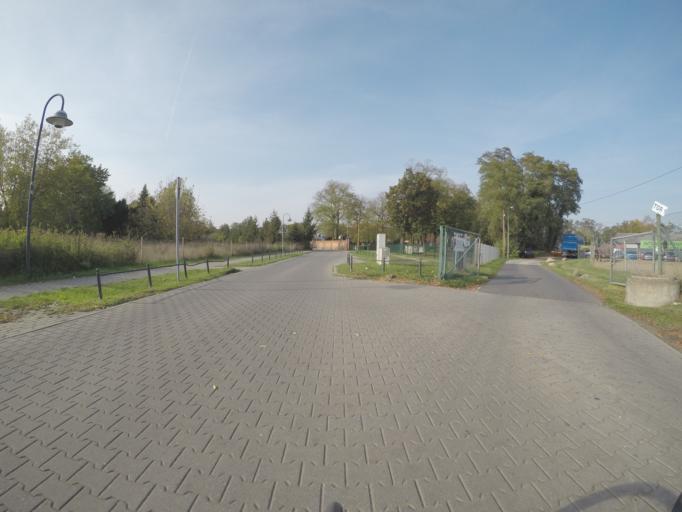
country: DE
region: Berlin
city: Gropiusstadt
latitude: 52.3984
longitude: 13.4456
